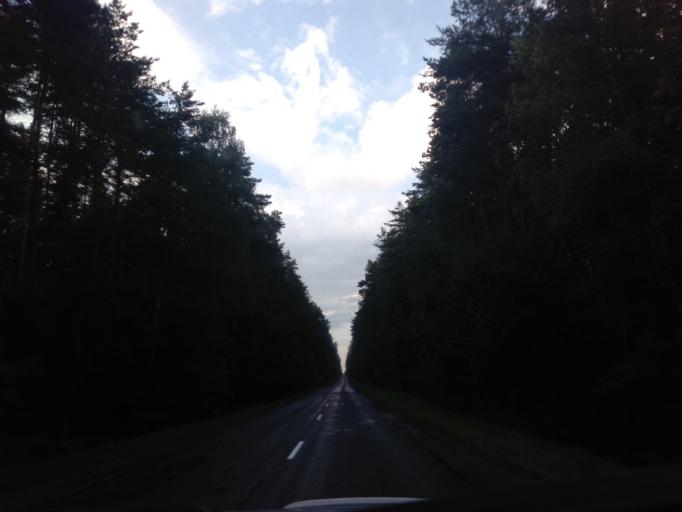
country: BY
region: Minsk
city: Uzda
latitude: 53.3603
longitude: 27.1002
